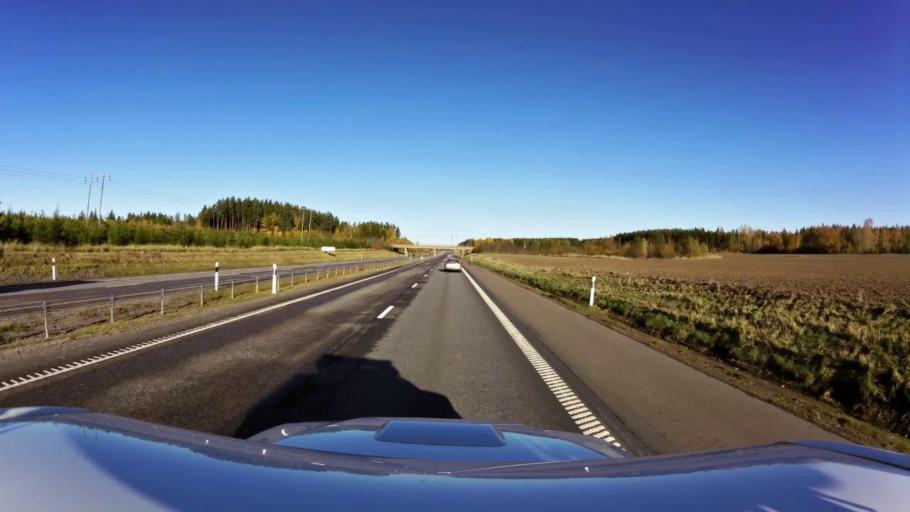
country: SE
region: OEstergoetland
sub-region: Linkopings Kommun
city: Malmslatt
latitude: 58.4129
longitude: 15.5469
